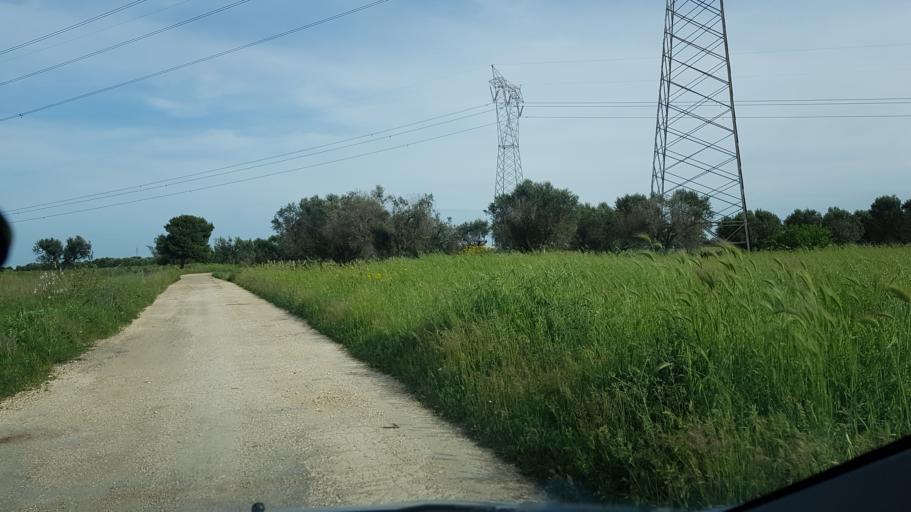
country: IT
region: Apulia
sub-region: Provincia di Brindisi
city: Tuturano
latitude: 40.5535
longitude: 17.9299
